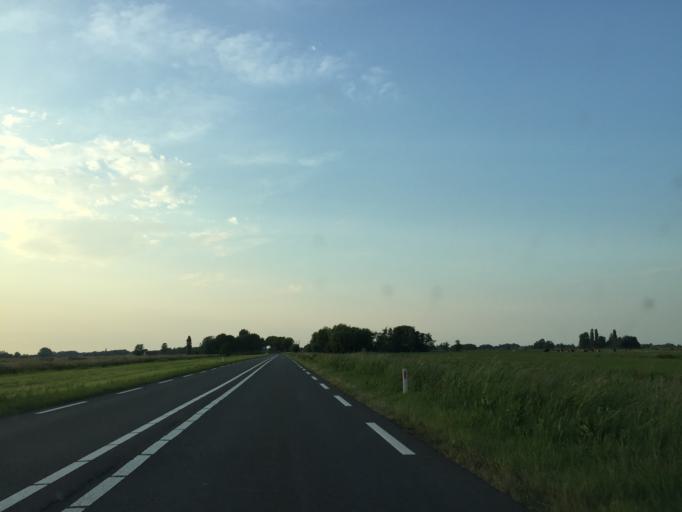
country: NL
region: South Holland
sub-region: Gemeente Vlist
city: Vlist
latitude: 51.9467
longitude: 4.7802
